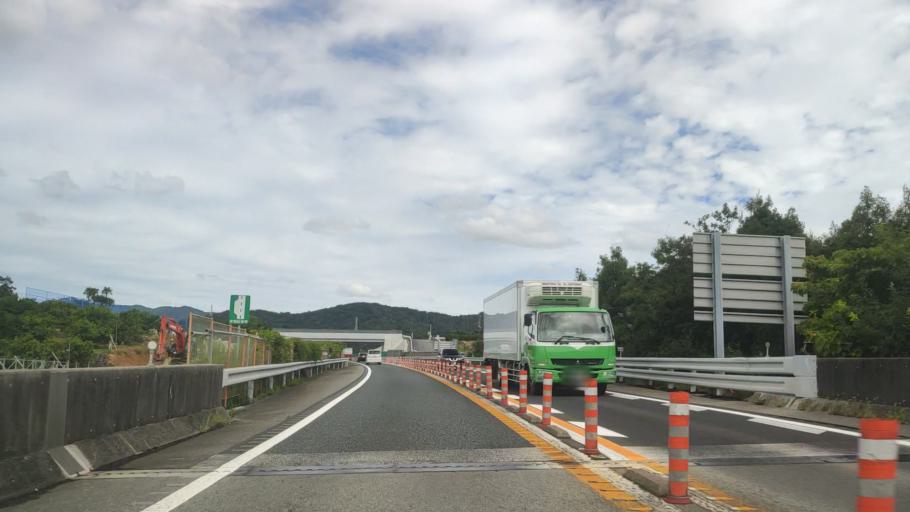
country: JP
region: Wakayama
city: Gobo
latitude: 33.9074
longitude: 135.1935
